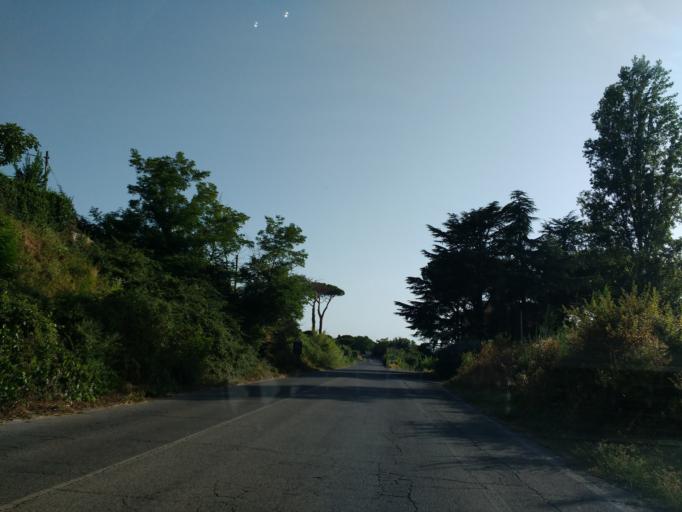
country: IT
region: Latium
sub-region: Citta metropolitana di Roma Capitale
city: Marino
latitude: 41.7558
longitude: 12.6388
